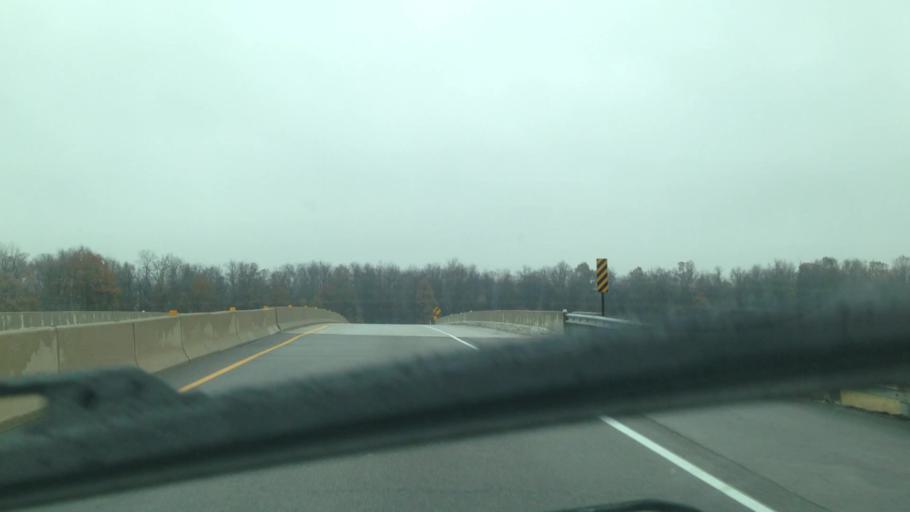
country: US
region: Indiana
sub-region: Saint Joseph County
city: Granger
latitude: 41.7324
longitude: -86.1418
